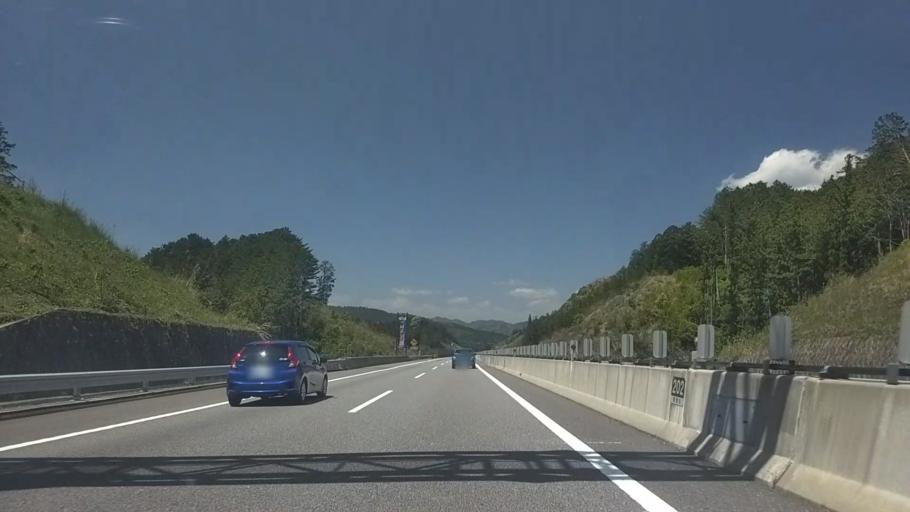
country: JP
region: Aichi
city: Shinshiro
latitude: 34.8993
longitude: 137.6222
